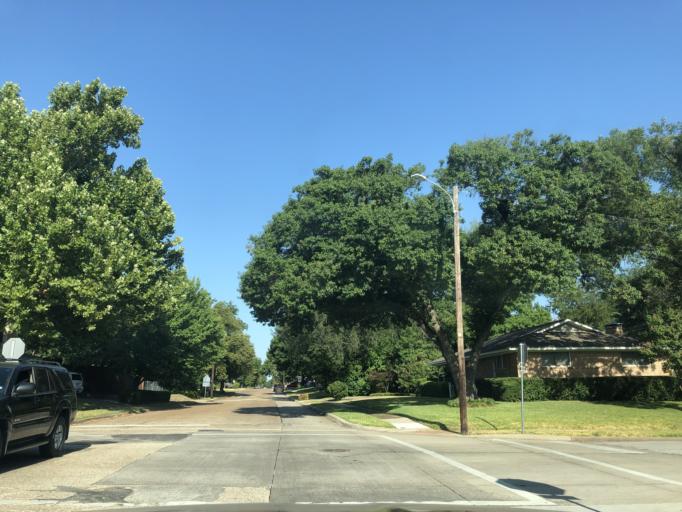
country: US
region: Texas
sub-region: Dallas County
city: Garland
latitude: 32.8710
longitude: -96.6432
